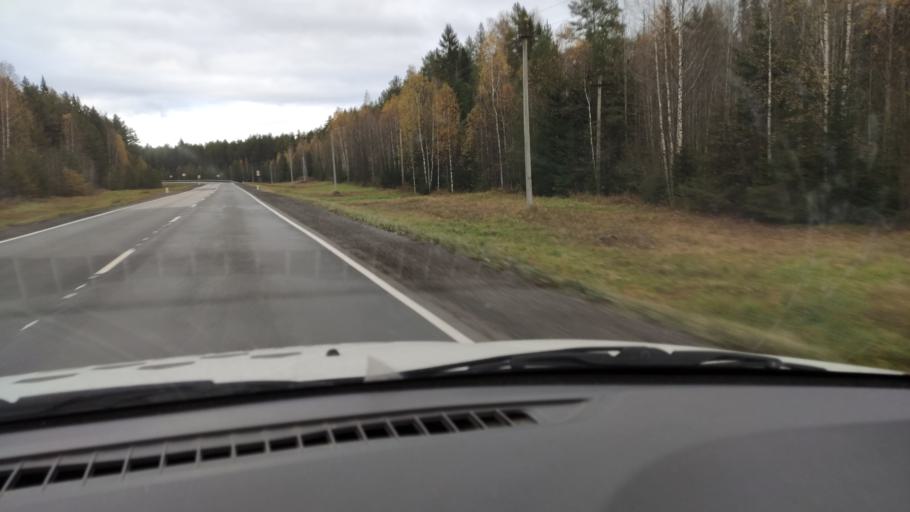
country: RU
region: Kirov
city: Belaya Kholunitsa
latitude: 58.8319
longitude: 50.6860
